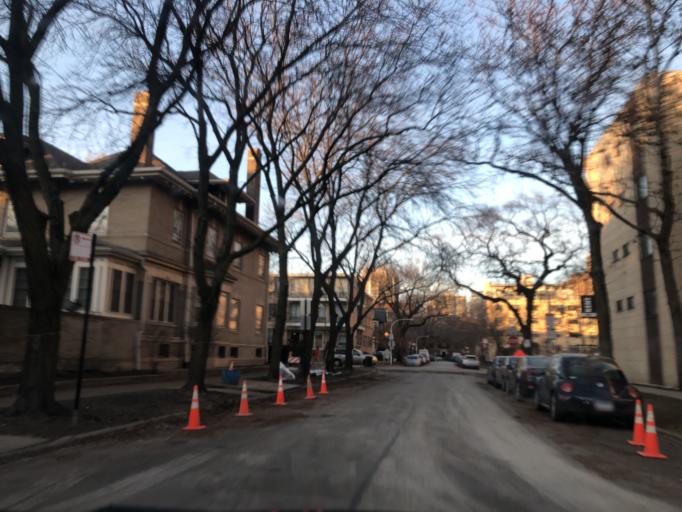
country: US
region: Illinois
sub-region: Cook County
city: Chicago
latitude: 41.9360
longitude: -87.6418
